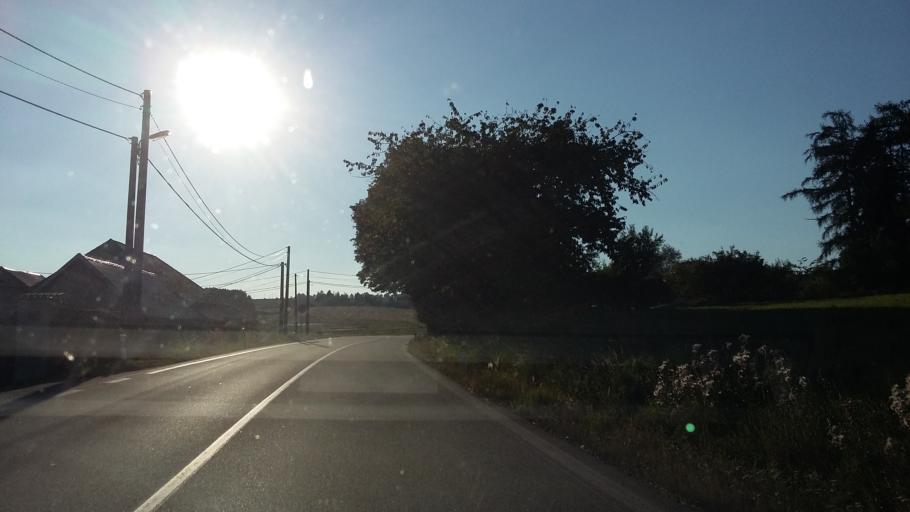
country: CZ
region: Vysocina
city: Velky Beranov
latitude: 49.3999
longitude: 15.6846
